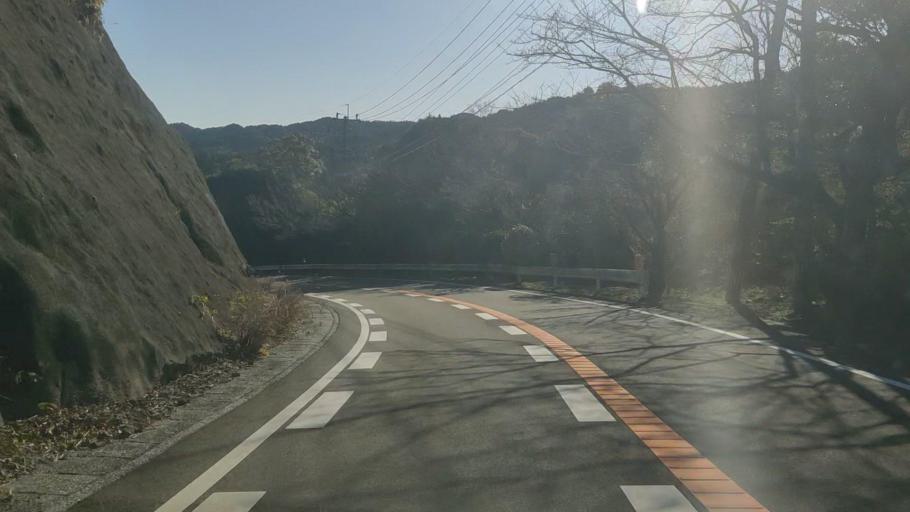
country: JP
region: Miyazaki
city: Nobeoka
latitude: 32.6310
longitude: 131.7340
